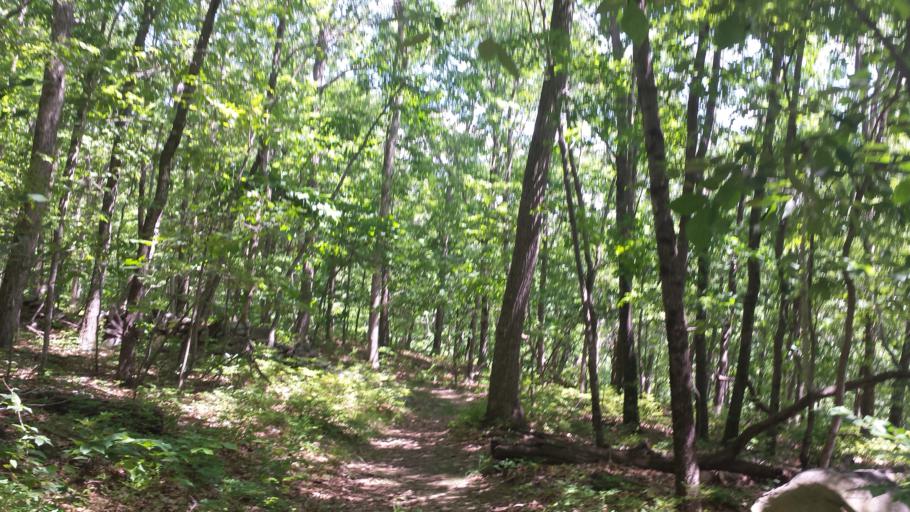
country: US
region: New York
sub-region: Westchester County
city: Pound Ridge
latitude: 41.2659
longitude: -73.5821
